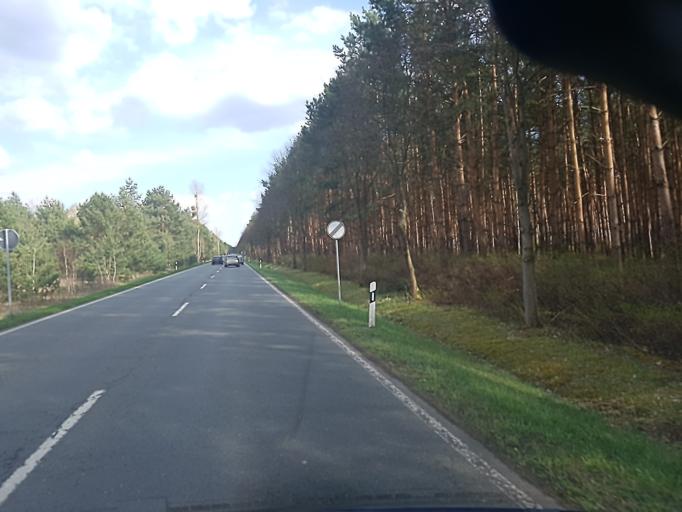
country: DE
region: Saxony-Anhalt
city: Zschornewitz
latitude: 51.6964
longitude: 12.4295
